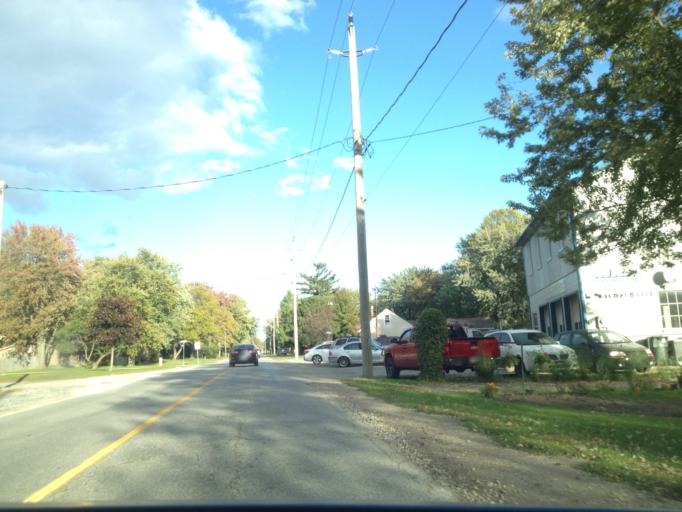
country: US
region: Michigan
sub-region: Wayne County
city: Grosse Pointe Farms
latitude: 42.2942
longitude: -82.7045
